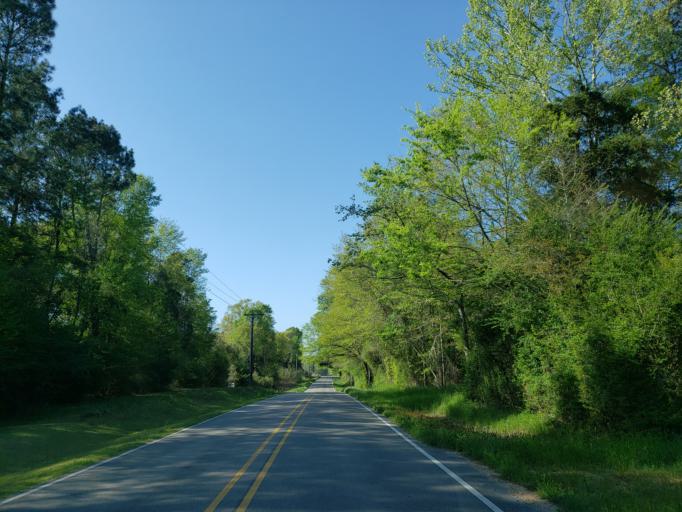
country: US
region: Mississippi
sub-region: Jones County
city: Ellisville
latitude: 31.5711
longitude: -89.3700
